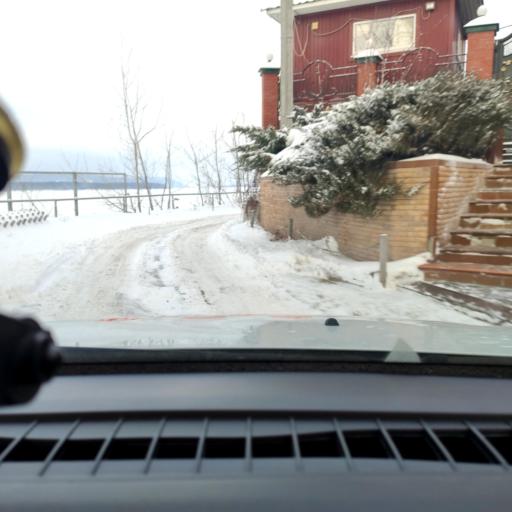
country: RU
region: Samara
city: Samara
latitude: 53.2833
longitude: 50.1896
